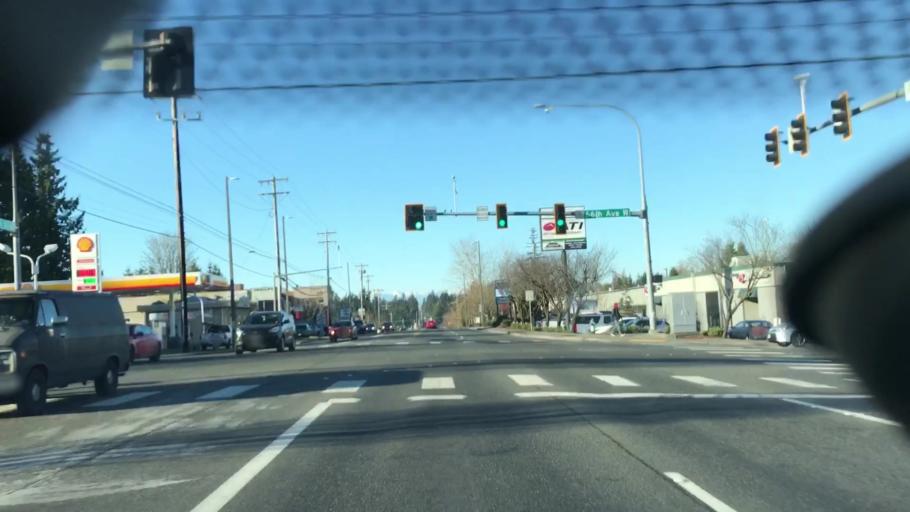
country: US
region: Washington
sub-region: Snohomish County
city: Mountlake Terrace
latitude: 47.7995
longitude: -122.3216
